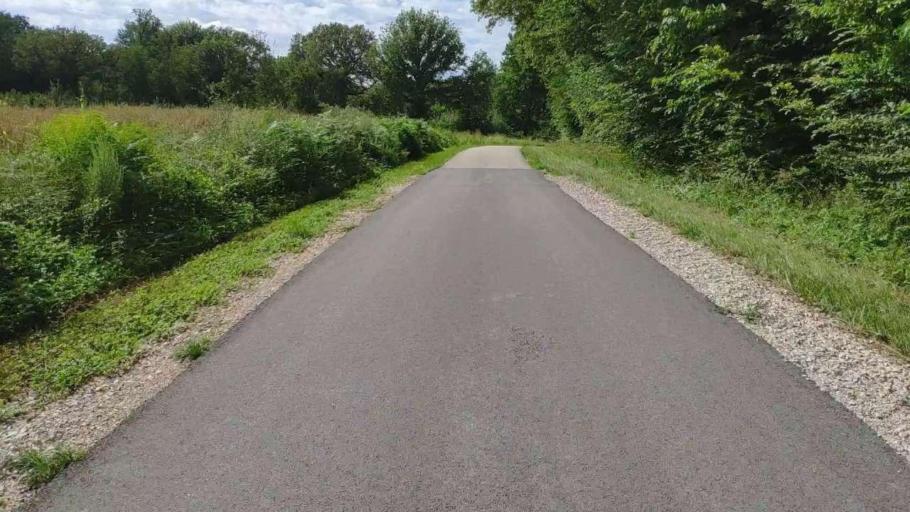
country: FR
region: Franche-Comte
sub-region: Departement du Jura
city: Bletterans
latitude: 46.8078
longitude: 5.4419
